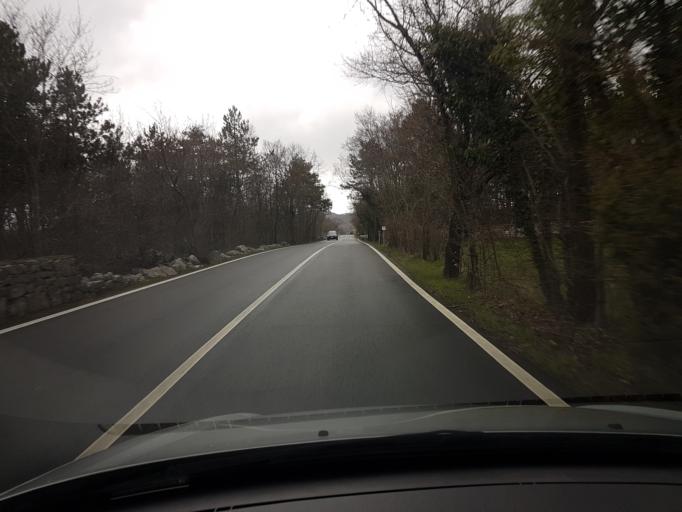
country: IT
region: Friuli Venezia Giulia
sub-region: Provincia di Trieste
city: Sgonico
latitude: 45.7428
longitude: 13.7219
